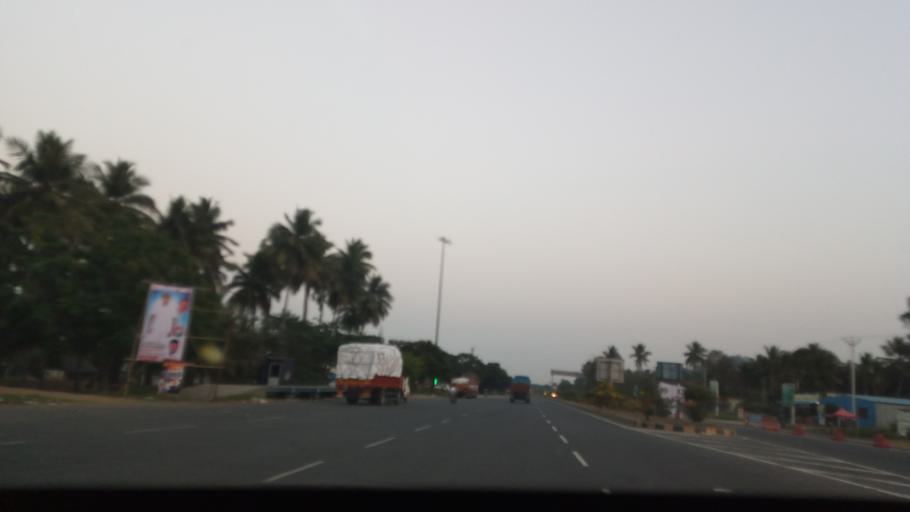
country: IN
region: Tamil Nadu
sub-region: Salem
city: Belur
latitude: 11.6613
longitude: 78.3313
